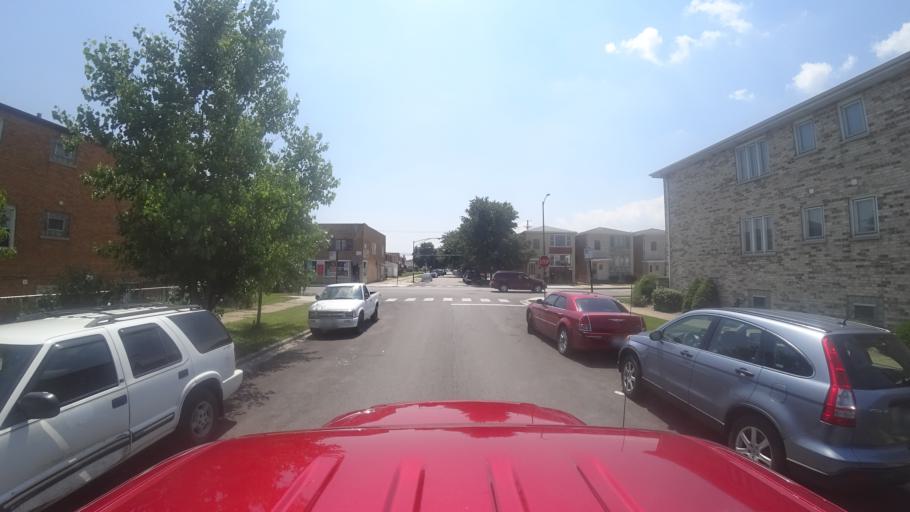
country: US
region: Illinois
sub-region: Cook County
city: Cicero
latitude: 41.7934
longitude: -87.7342
